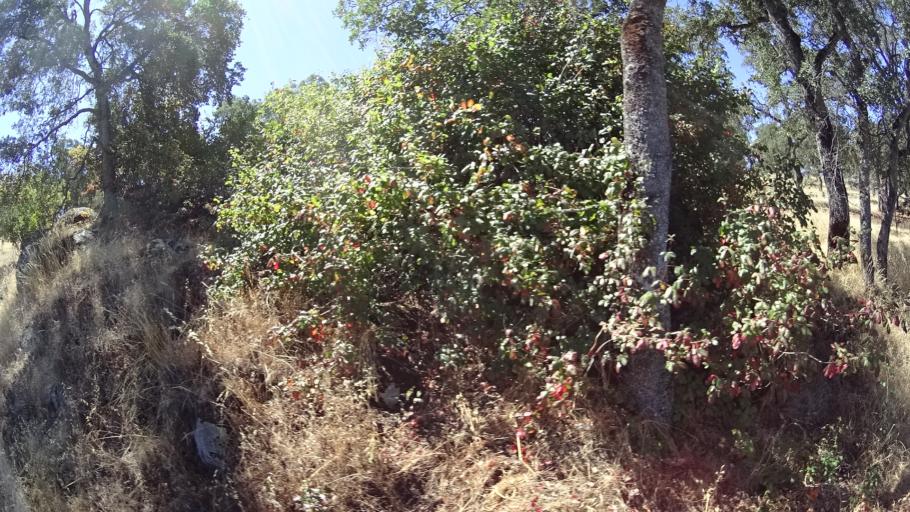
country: US
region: California
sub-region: Calaveras County
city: Copperopolis
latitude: 37.9404
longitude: -120.7298
